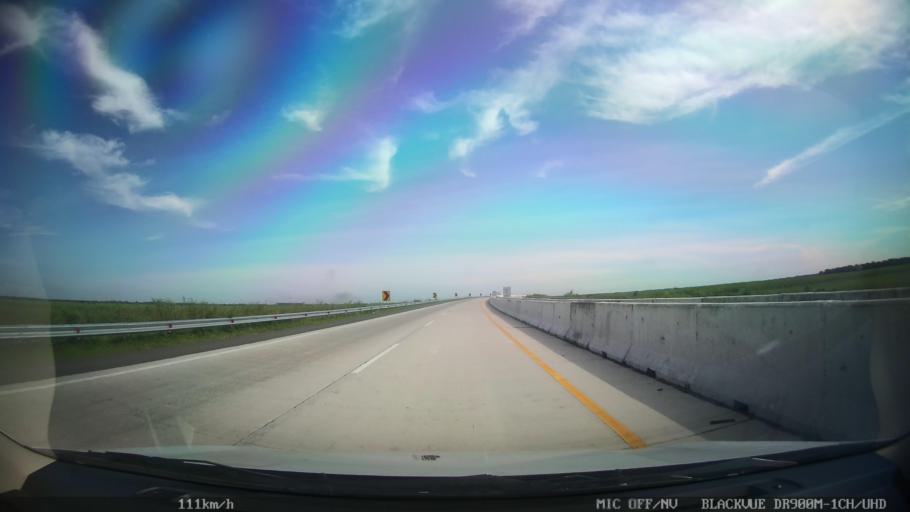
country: ID
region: North Sumatra
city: Binjai
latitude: 3.6611
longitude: 98.5325
